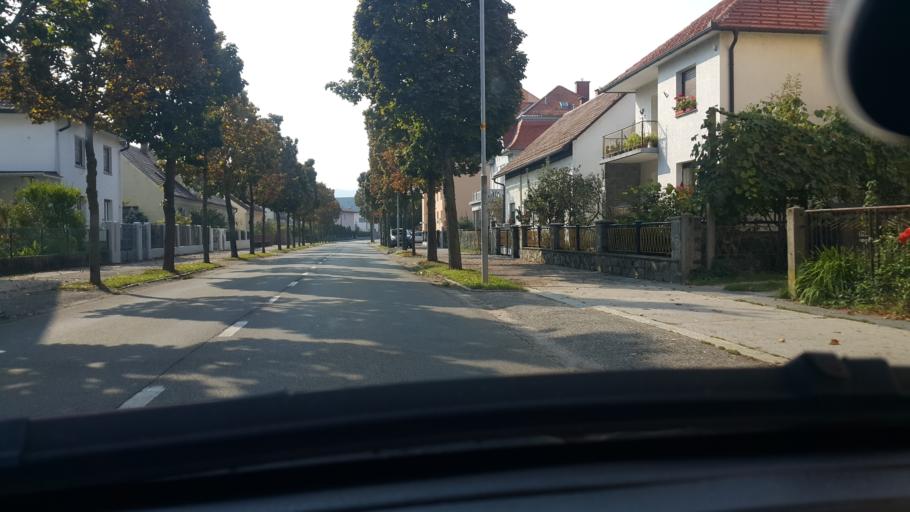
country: SI
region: Maribor
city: Maribor
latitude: 46.5485
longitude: 15.6364
